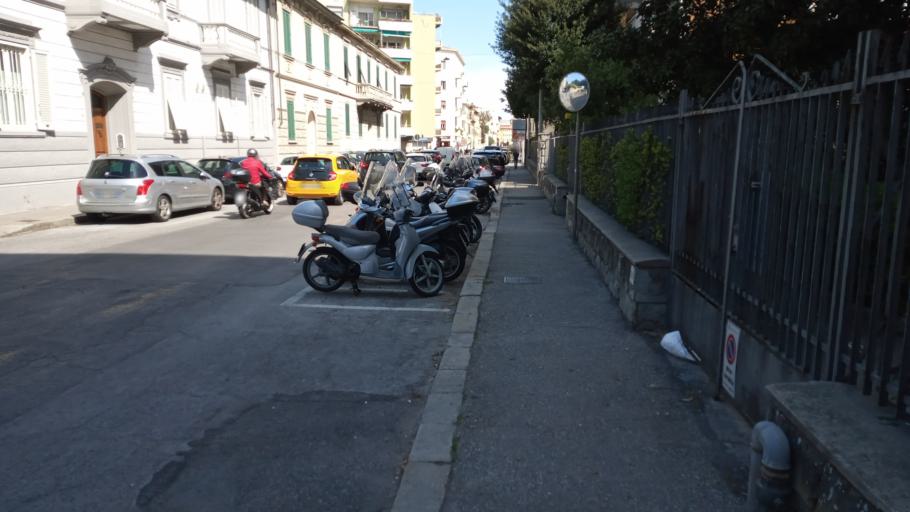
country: IT
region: Tuscany
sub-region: Provincia di Livorno
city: Livorno
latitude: 43.5397
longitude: 10.3127
